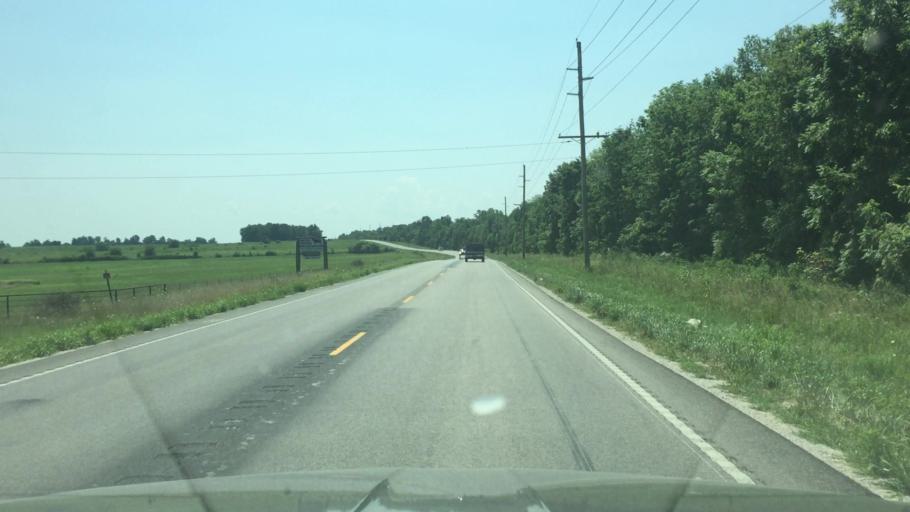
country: US
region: Missouri
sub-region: Miller County
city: Eldon
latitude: 38.3910
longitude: -92.7071
